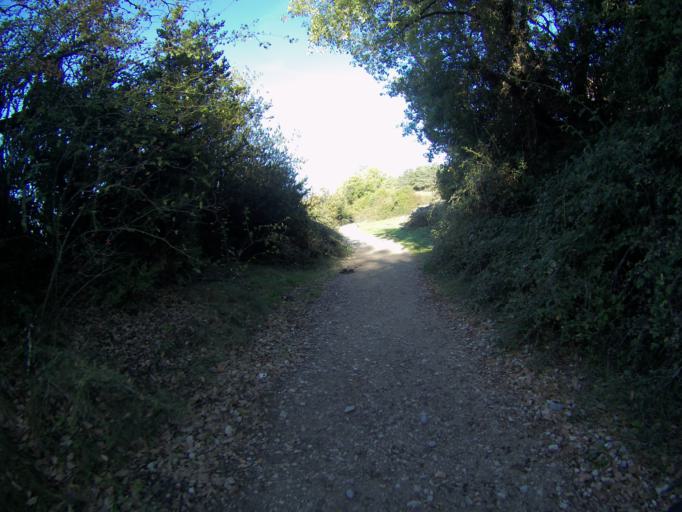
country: ES
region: Navarre
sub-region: Provincia de Navarra
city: Lizoain
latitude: 42.9374
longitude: -1.4773
